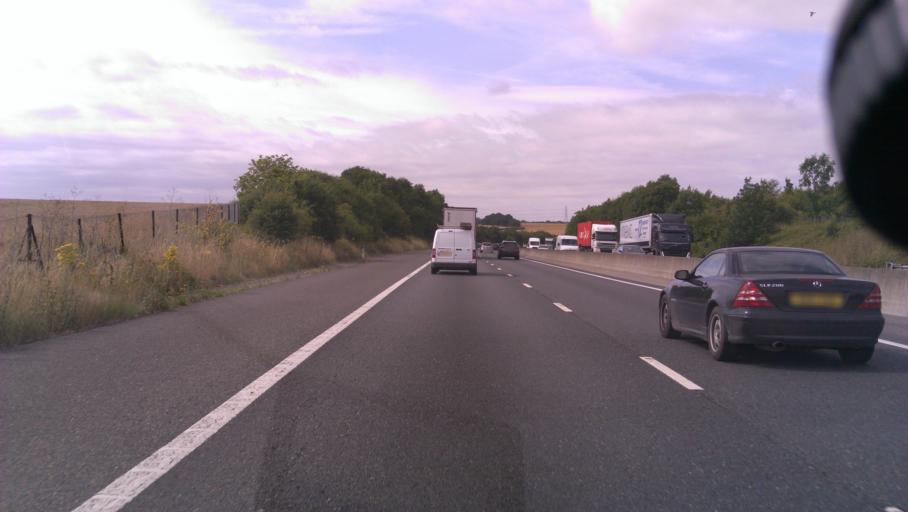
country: GB
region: England
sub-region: Essex
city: Saffron Walden
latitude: 51.9765
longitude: 0.2063
